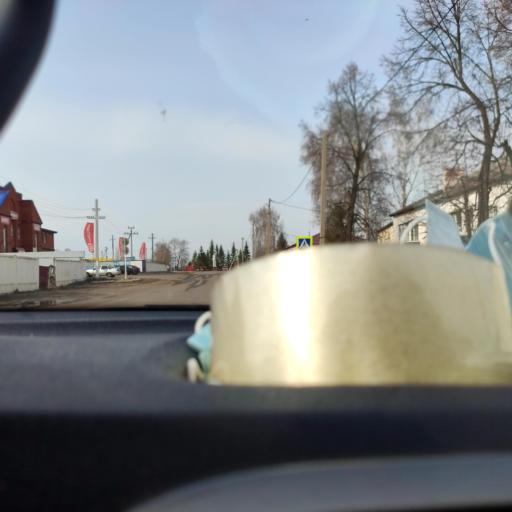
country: RU
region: Bashkortostan
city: Ulukulevo
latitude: 54.3776
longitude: 56.4496
